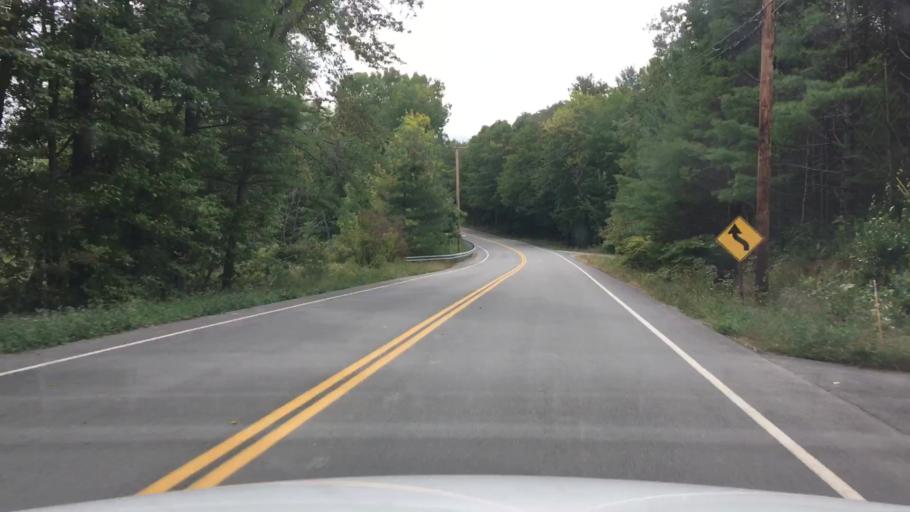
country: US
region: Maine
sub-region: Penobscot County
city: Milford
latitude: 44.9581
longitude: -68.6976
